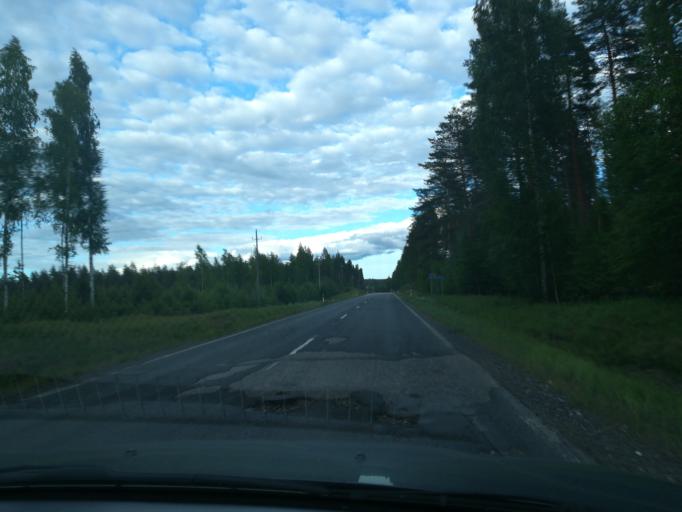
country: FI
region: Southern Savonia
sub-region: Mikkeli
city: Puumala
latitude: 61.5602
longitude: 28.0208
